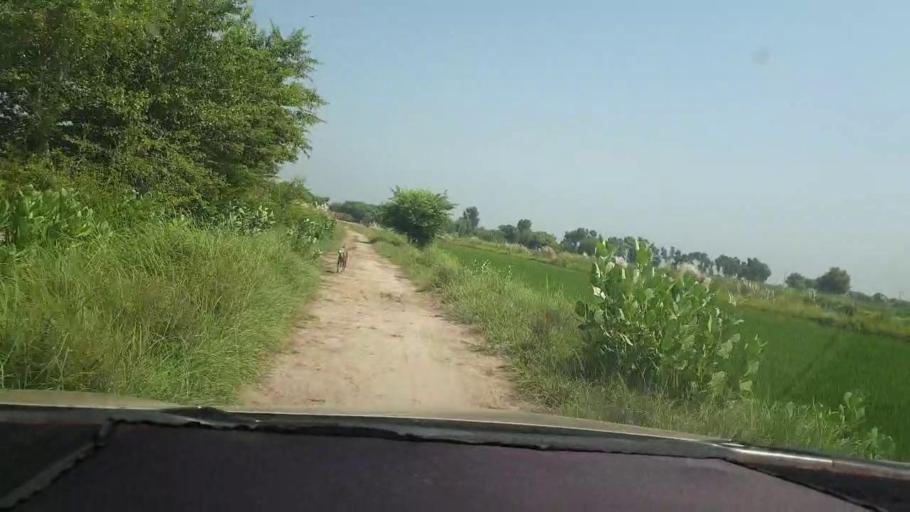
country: PK
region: Sindh
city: Kambar
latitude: 27.6069
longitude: 68.0652
